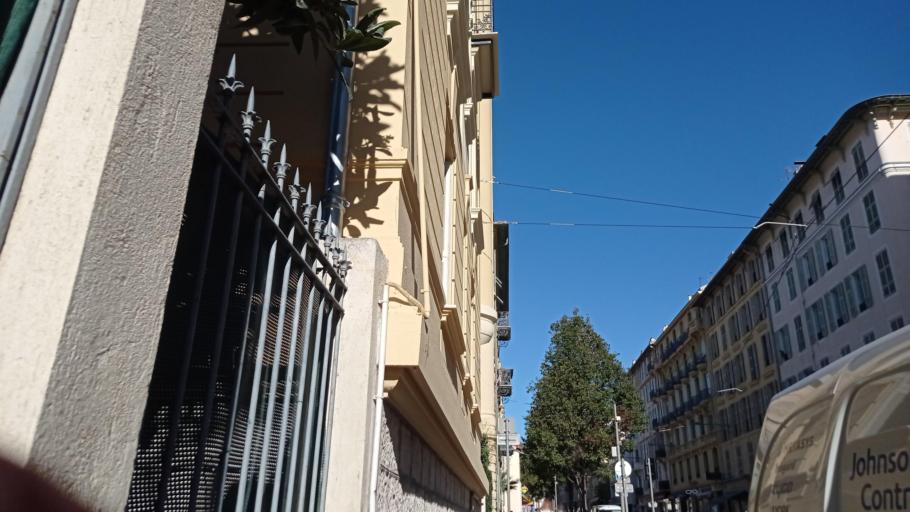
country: FR
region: Provence-Alpes-Cote d'Azur
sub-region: Departement des Alpes-Maritimes
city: Nice
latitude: 43.7120
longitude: 7.2617
